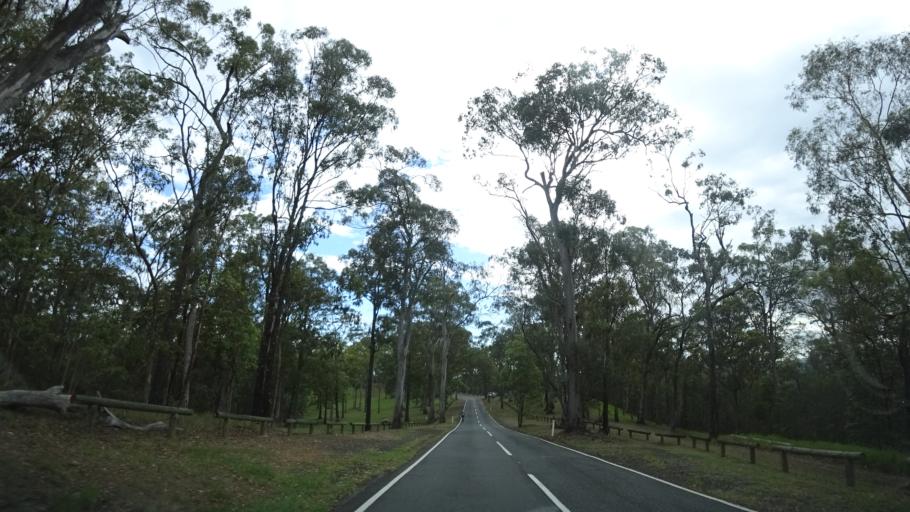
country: AU
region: Queensland
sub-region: Brisbane
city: Kenmore Hills
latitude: -27.4689
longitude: 152.9427
